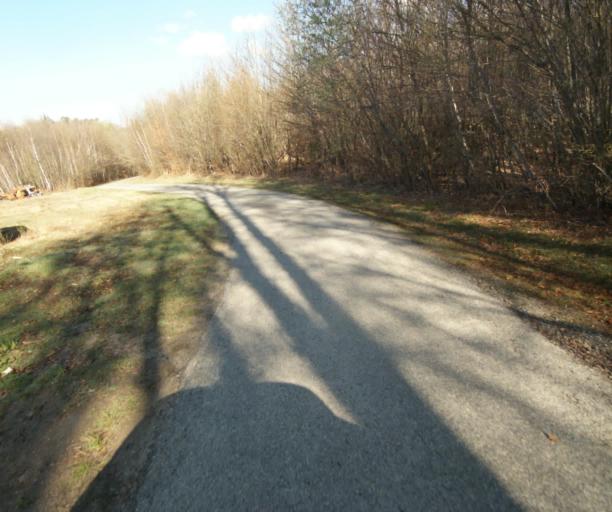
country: FR
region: Limousin
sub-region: Departement de la Correze
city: Laguenne
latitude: 45.2353
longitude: 1.9185
